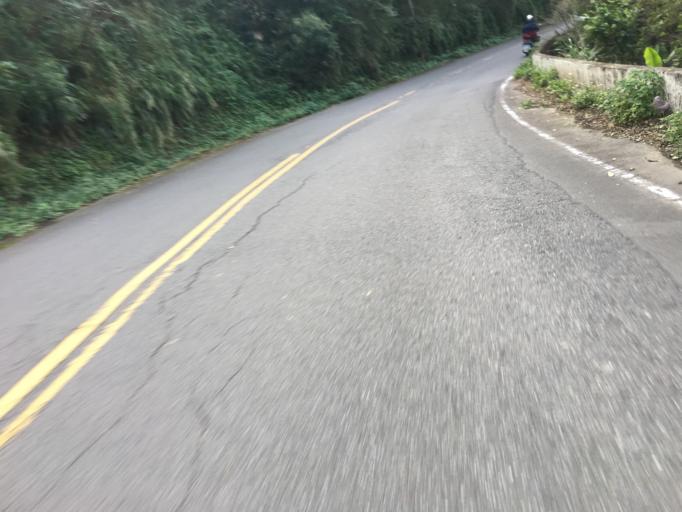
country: TW
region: Taiwan
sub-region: Hsinchu
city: Hsinchu
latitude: 24.7381
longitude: 121.0321
